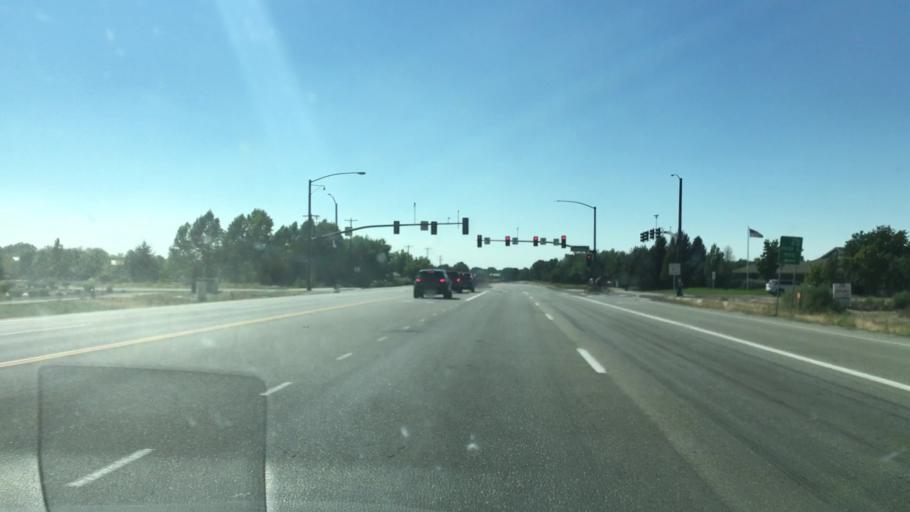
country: US
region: Idaho
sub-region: Ada County
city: Eagle
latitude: 43.6877
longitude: -116.3331
